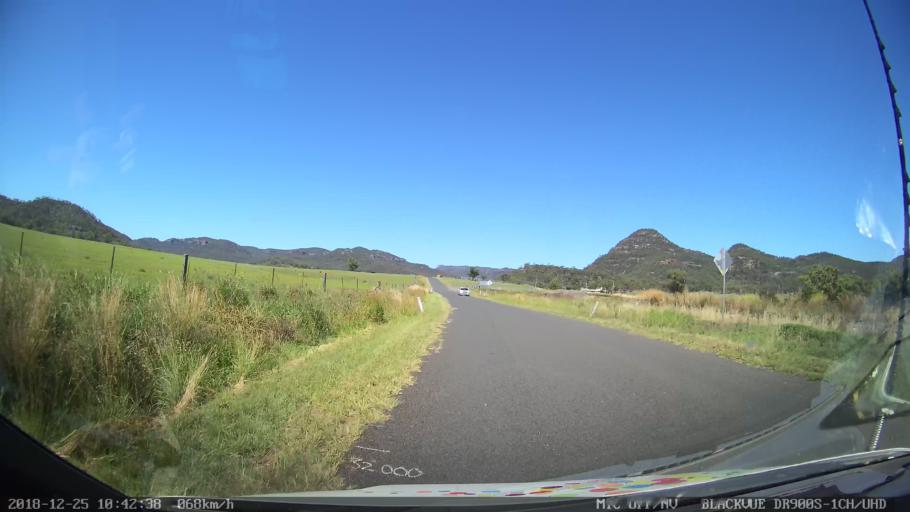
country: AU
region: New South Wales
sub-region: Upper Hunter Shire
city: Merriwa
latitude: -32.4169
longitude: 150.3209
